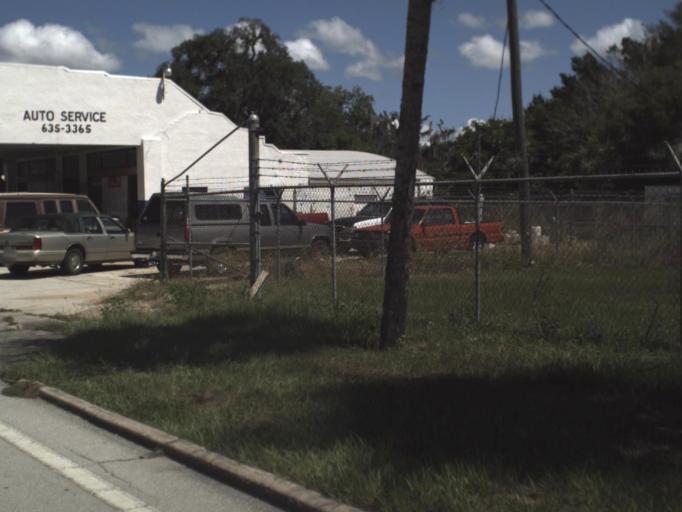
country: US
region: Florida
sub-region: Polk County
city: Frostproof
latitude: 27.7419
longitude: -81.5305
